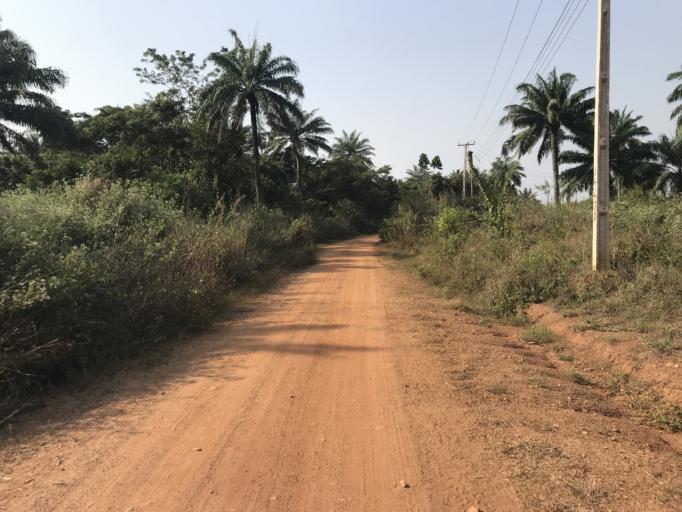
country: NG
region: Osun
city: Olupona
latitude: 7.6064
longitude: 4.1446
